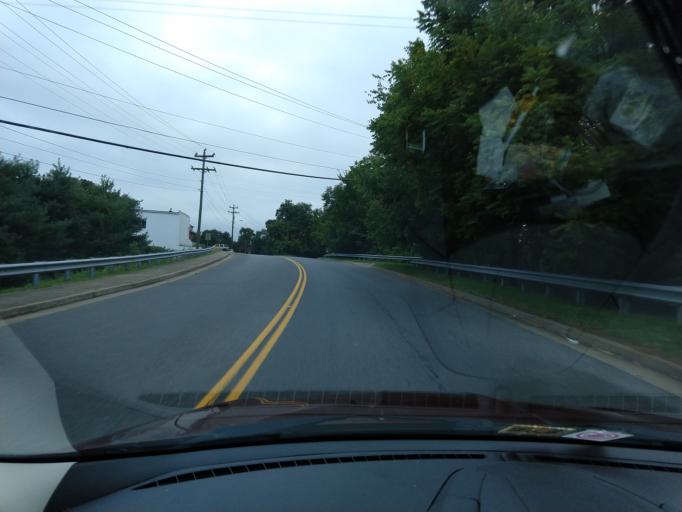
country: US
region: Virginia
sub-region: City of Covington
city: Fairlawn
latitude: 37.7612
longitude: -79.9888
